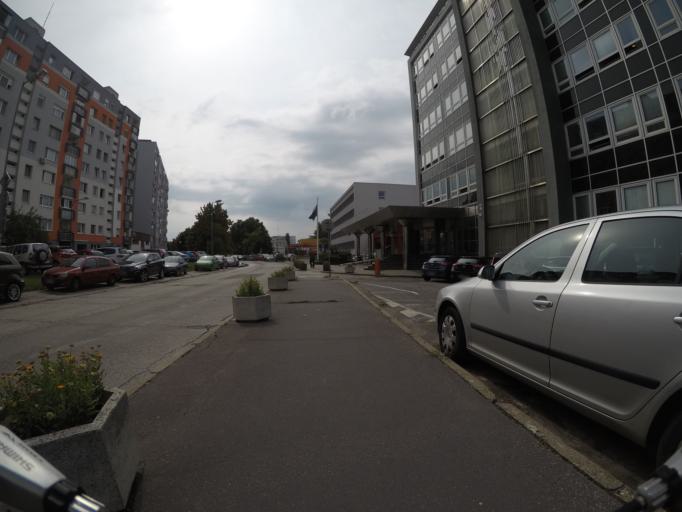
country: SK
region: Bratislavsky
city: Bratislava
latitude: 48.1479
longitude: 17.1580
